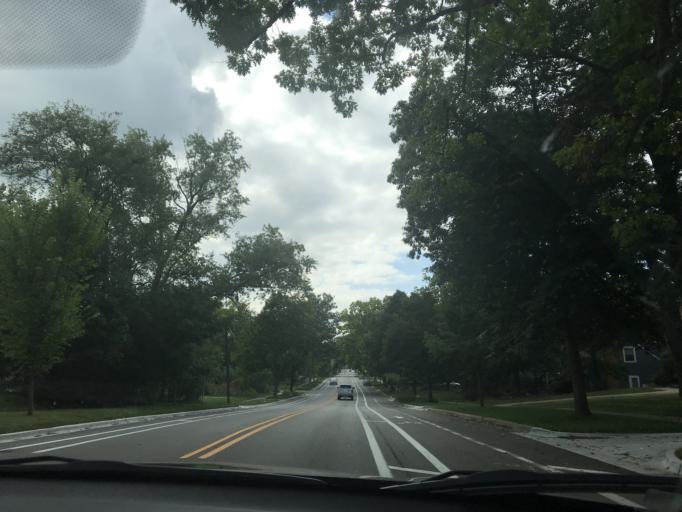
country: US
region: Michigan
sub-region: Washtenaw County
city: Ann Arbor
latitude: 42.2684
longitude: -83.7594
